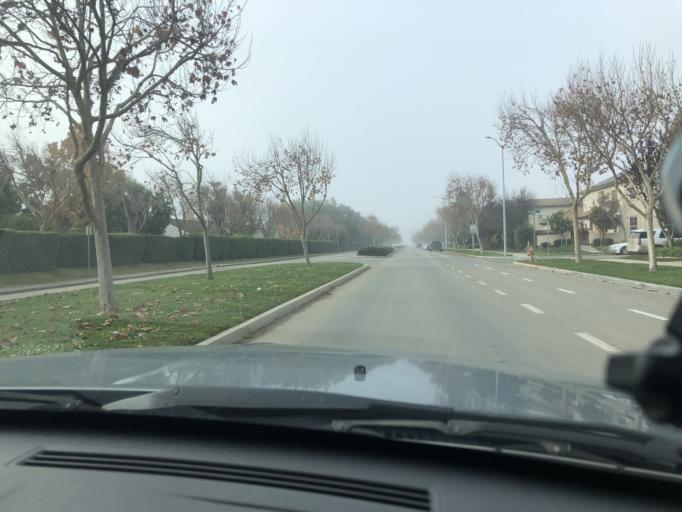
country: US
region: California
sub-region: Monterey County
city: King City
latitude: 36.2188
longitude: -121.1333
